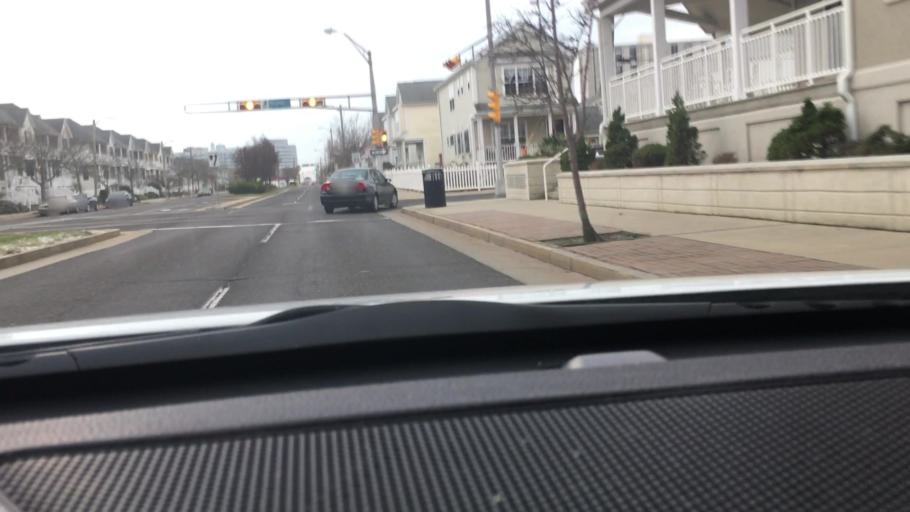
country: US
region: New Jersey
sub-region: Atlantic County
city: Atlantic City
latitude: 39.3713
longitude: -74.4151
